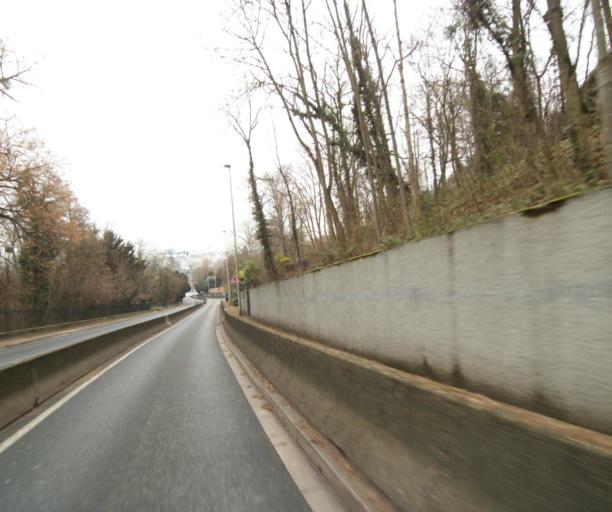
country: FR
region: Ile-de-France
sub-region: Departement des Yvelines
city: Bougival
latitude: 48.8664
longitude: 2.1548
